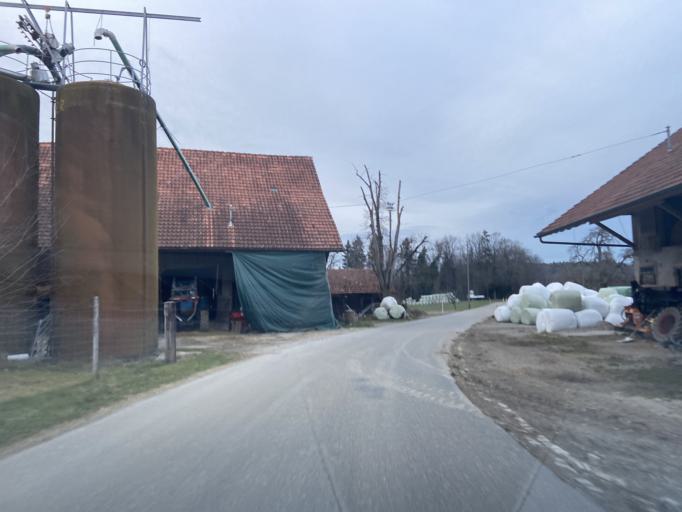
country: CH
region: Zurich
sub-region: Bezirk Winterthur
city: Wuelflingen (Kreis 6) / Niederfeld
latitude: 47.4933
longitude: 8.6654
